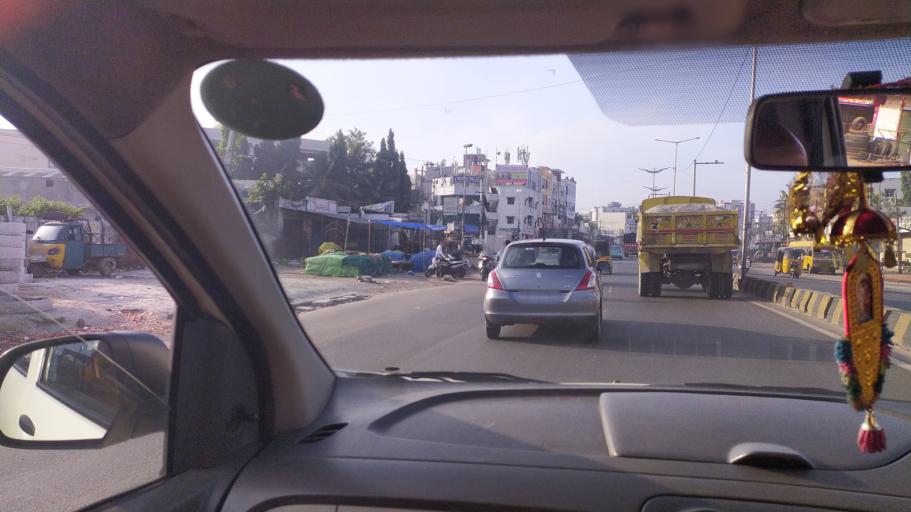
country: IN
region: Telangana
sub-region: Rangareddi
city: Balapur
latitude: 17.3175
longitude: 78.4666
